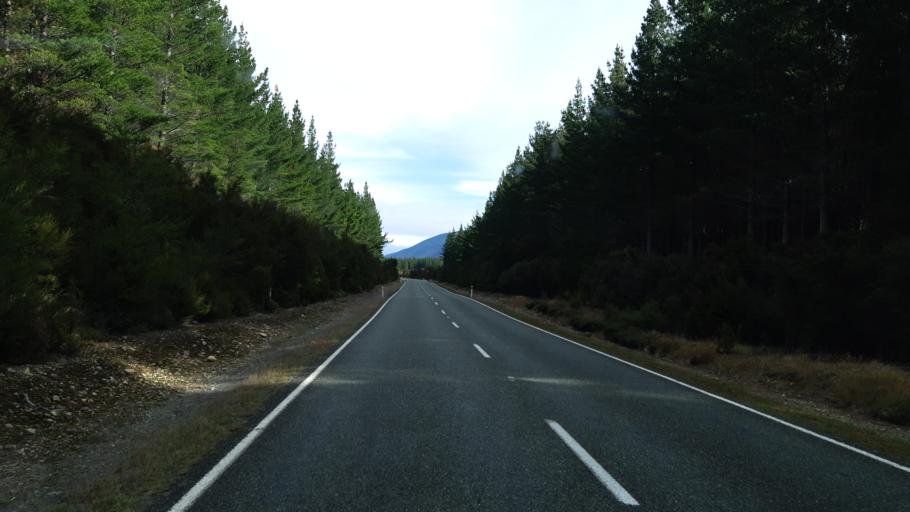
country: NZ
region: Tasman
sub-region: Tasman District
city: Wakefield
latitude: -41.7209
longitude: 173.0616
